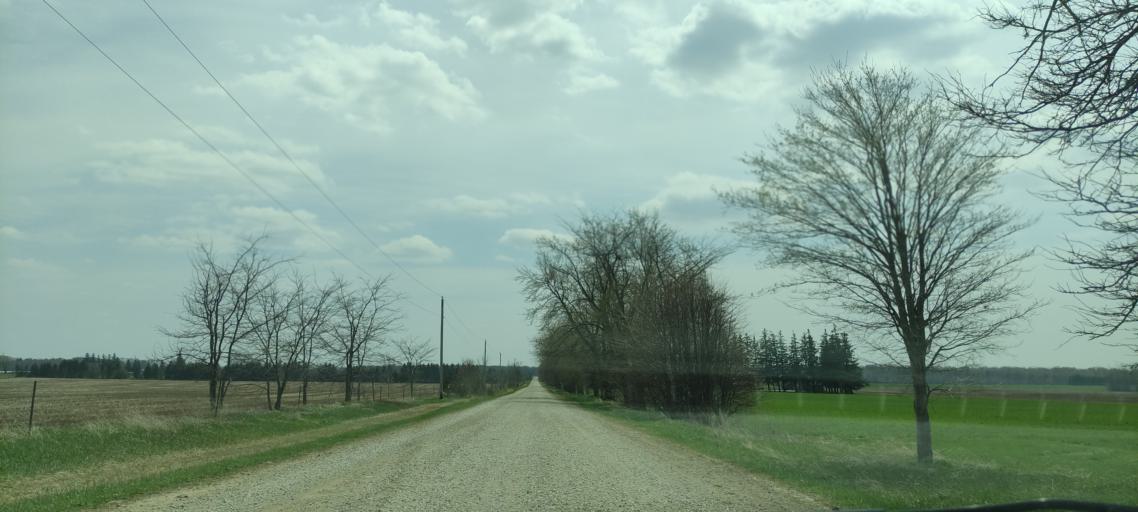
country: CA
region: Ontario
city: Stratford
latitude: 43.3434
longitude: -80.7420
